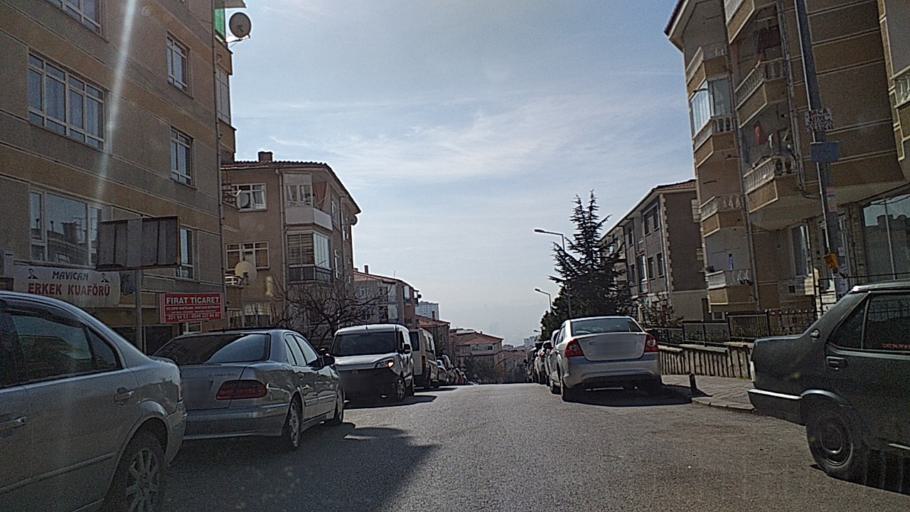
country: TR
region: Ankara
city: Ankara
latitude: 39.9816
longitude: 32.8297
